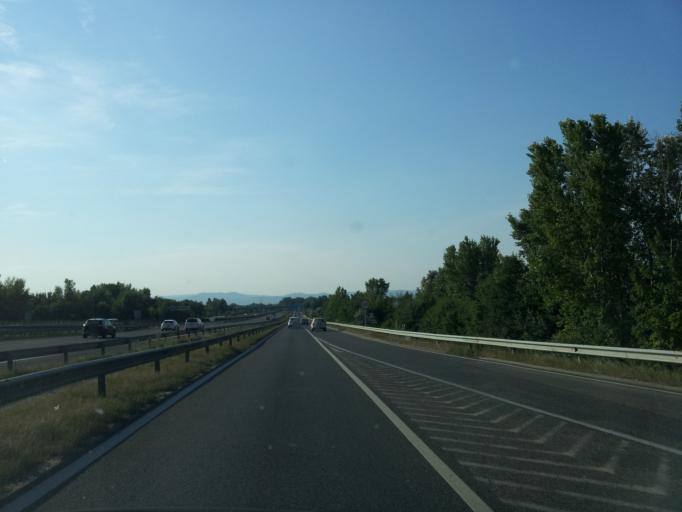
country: HU
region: Budapest
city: Budapest XV. keruelet
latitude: 47.5759
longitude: 19.1559
